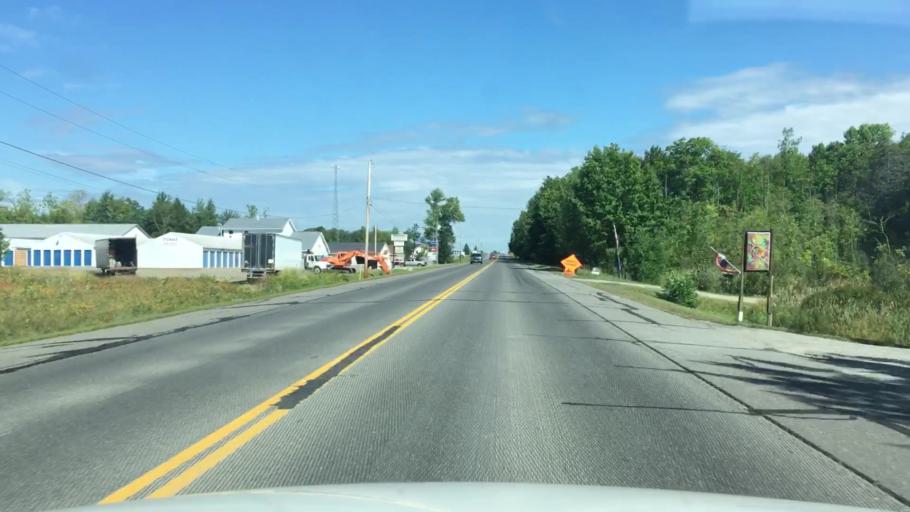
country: US
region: Maine
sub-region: Penobscot County
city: Newport
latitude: 44.8695
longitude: -69.2832
